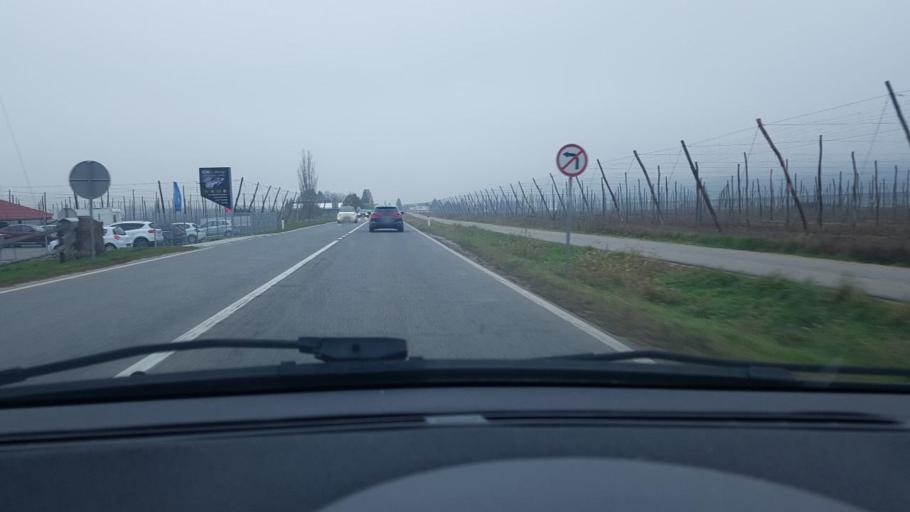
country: SI
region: Zalec
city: Zalec
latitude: 46.2444
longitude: 15.2030
